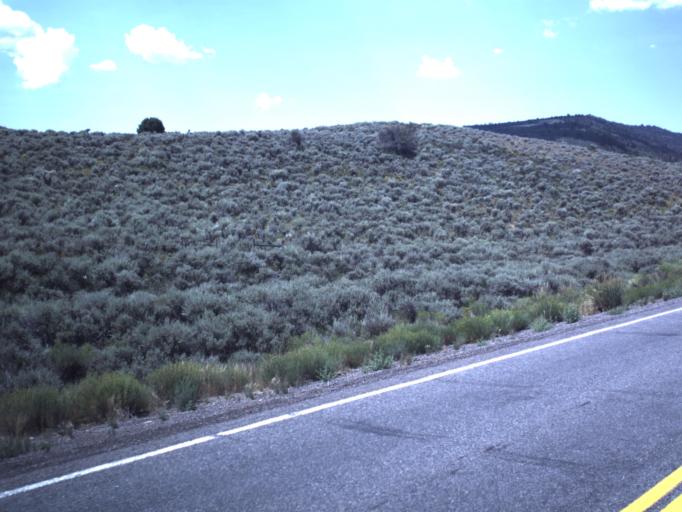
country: US
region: Utah
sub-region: Carbon County
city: Helper
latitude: 39.8608
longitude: -111.0423
